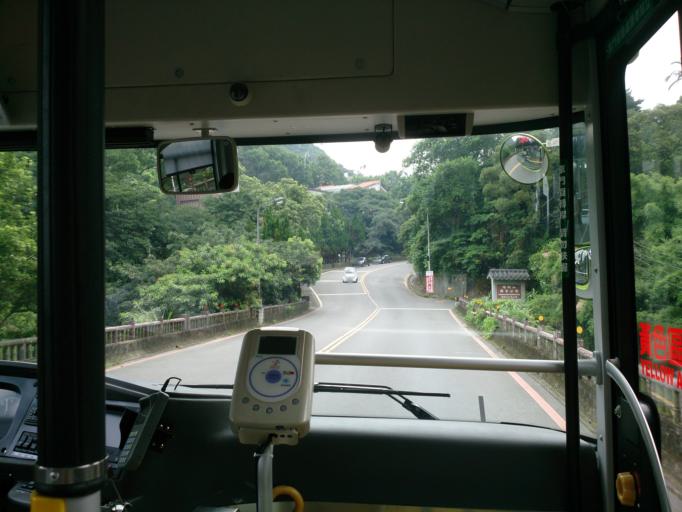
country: TW
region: Taipei
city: Taipei
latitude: 25.1462
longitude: 121.5495
